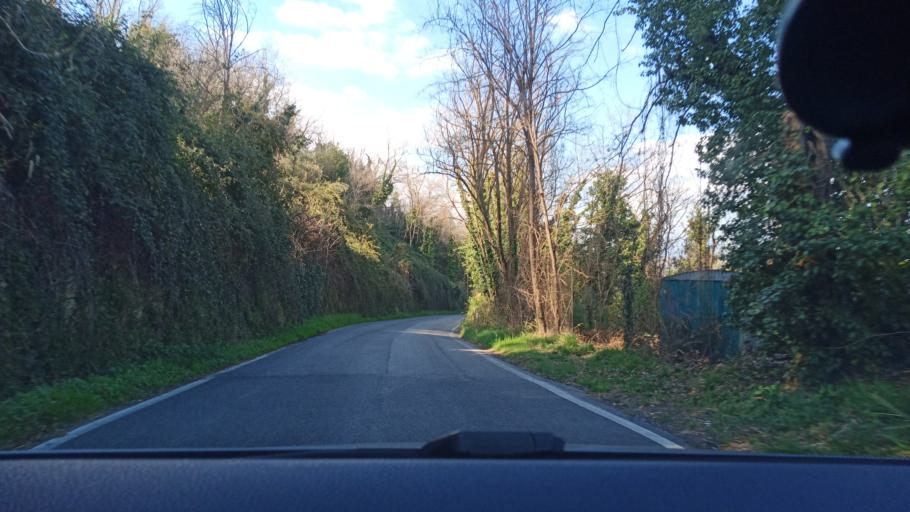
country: IT
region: Latium
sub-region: Citta metropolitana di Roma Capitale
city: Torrita Tiberina
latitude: 42.2457
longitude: 12.6186
